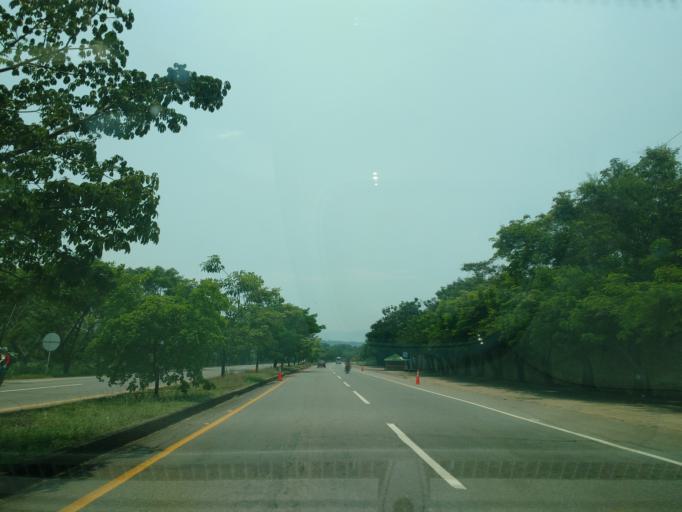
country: CO
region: Tolima
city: Melgar
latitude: 4.2120
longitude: -74.6784
